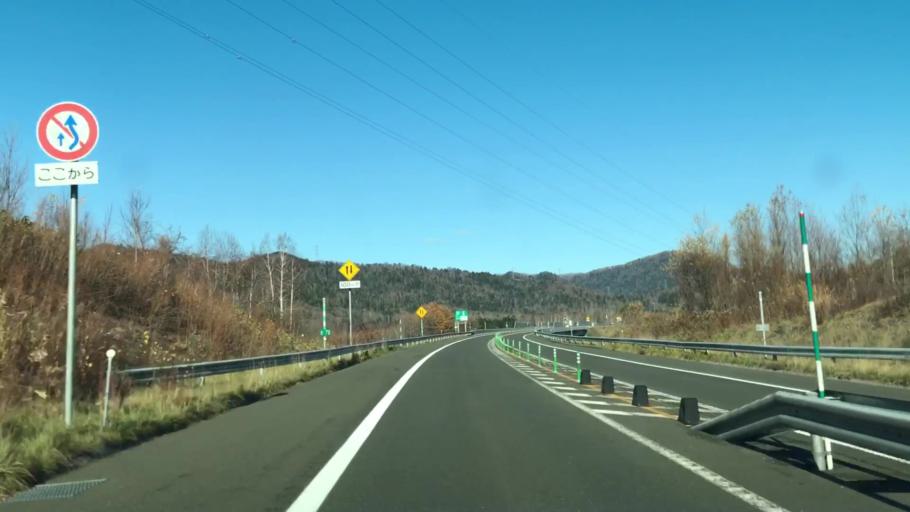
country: JP
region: Hokkaido
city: Shimo-furano
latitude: 43.0007
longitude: 142.4108
